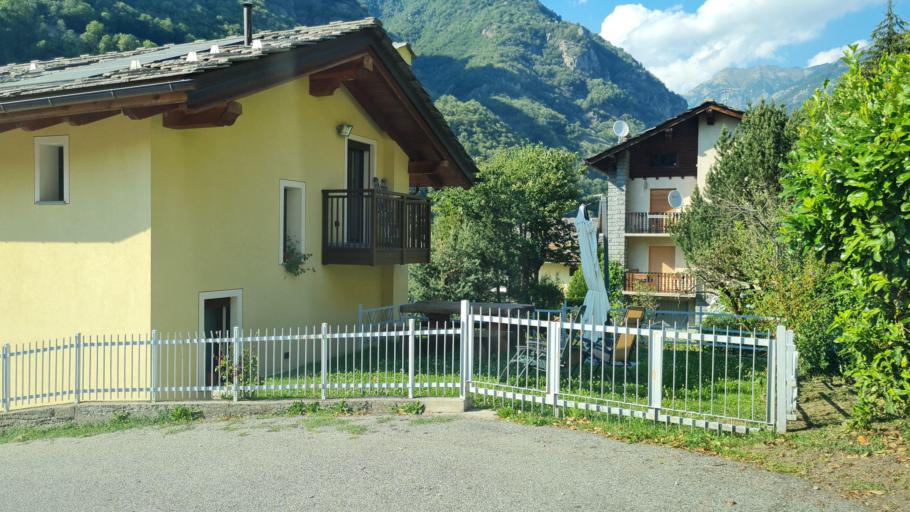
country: IT
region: Aosta Valley
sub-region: Valle d'Aosta
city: Lillianes
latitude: 45.6293
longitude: 7.8418
